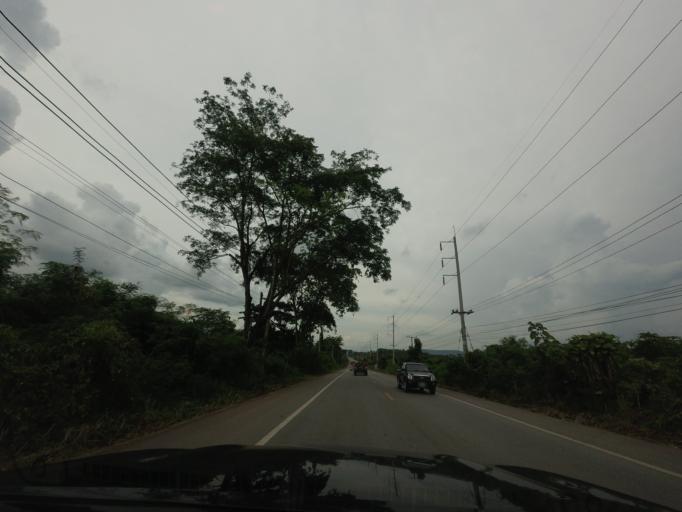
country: TH
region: Changwat Nong Bua Lamphu
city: Nong Bua Lamphu
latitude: 17.1506
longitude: 102.4159
